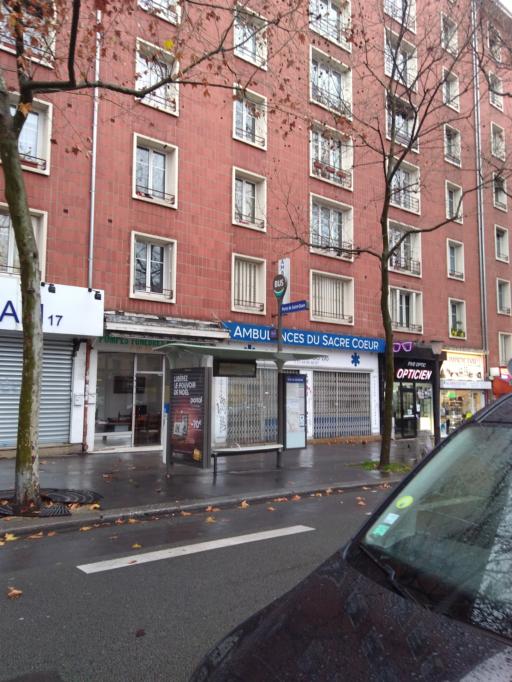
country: FR
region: Ile-de-France
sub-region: Paris
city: Saint-Ouen
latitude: 48.8983
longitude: 2.3291
